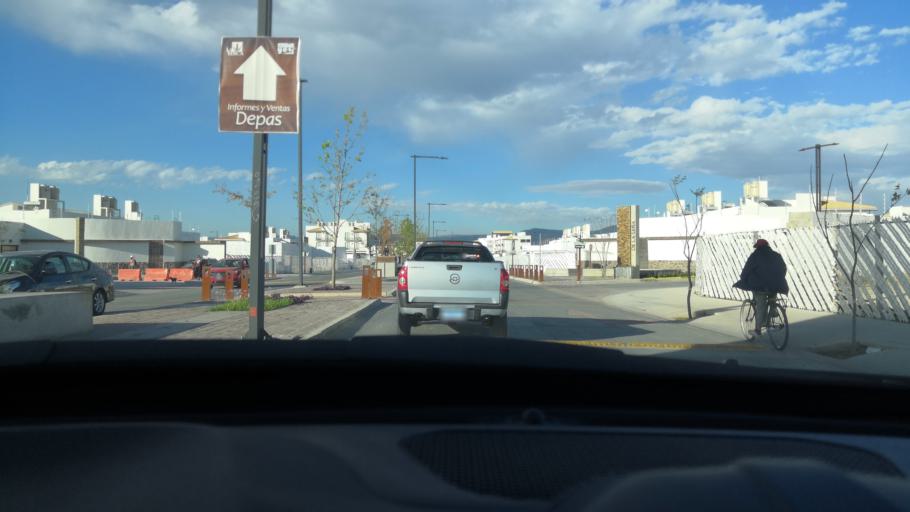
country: MX
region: Guanajuato
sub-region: Leon
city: San Jose de Duran (Los Troncoso)
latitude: 21.0836
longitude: -101.6539
